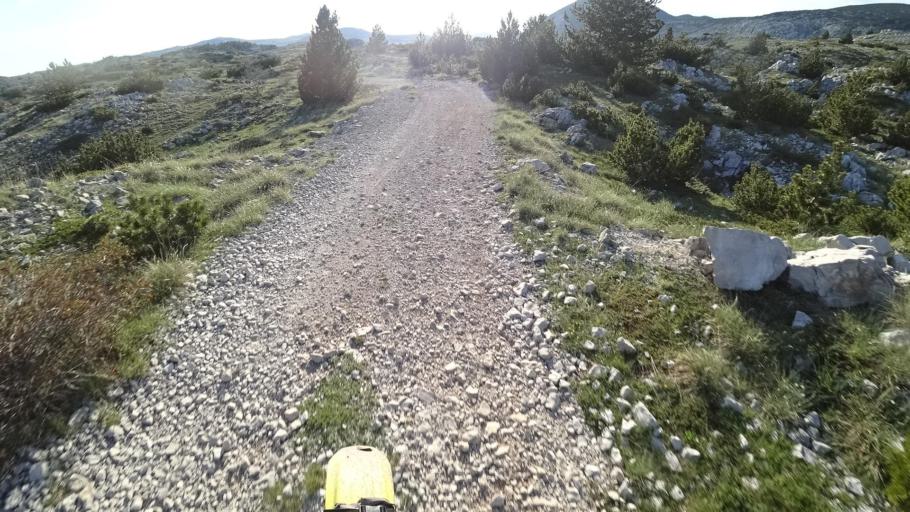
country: BA
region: Federation of Bosnia and Herzegovina
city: Kocerin
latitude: 43.5754
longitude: 17.5330
